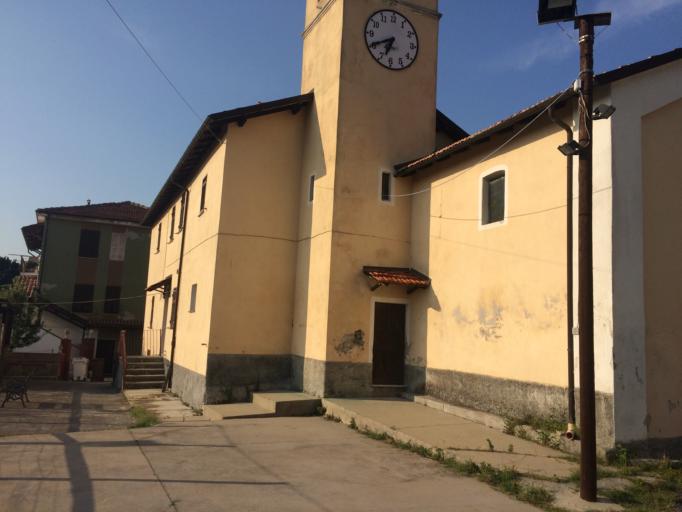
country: IT
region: Liguria
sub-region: Provincia di Savona
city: Giusvalla
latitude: 44.4467
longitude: 8.3534
